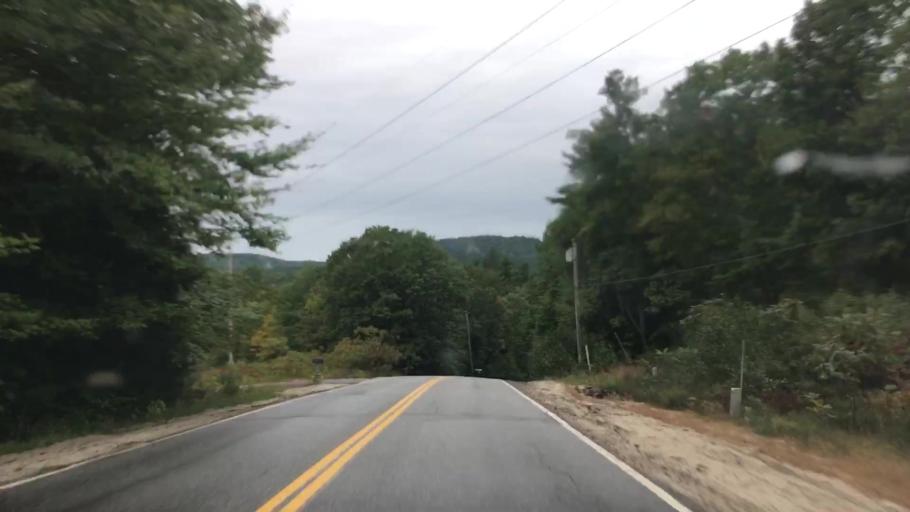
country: US
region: Maine
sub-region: Cumberland County
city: Raymond
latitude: 43.9448
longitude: -70.4602
